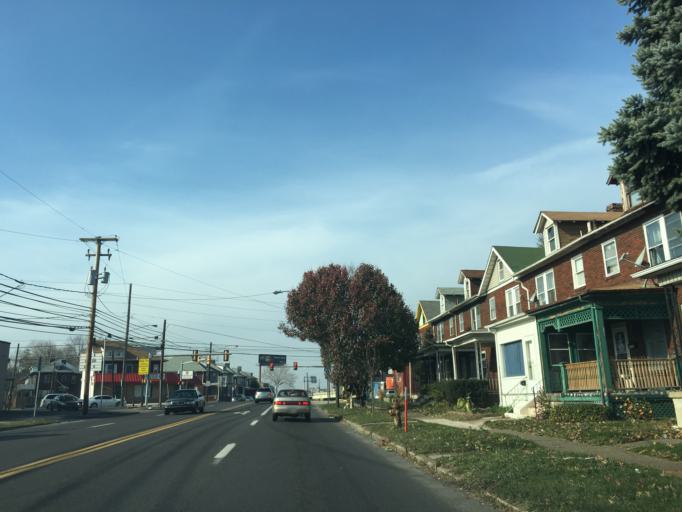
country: US
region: Pennsylvania
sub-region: Dauphin County
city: Penbrook
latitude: 40.2551
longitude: -76.8579
